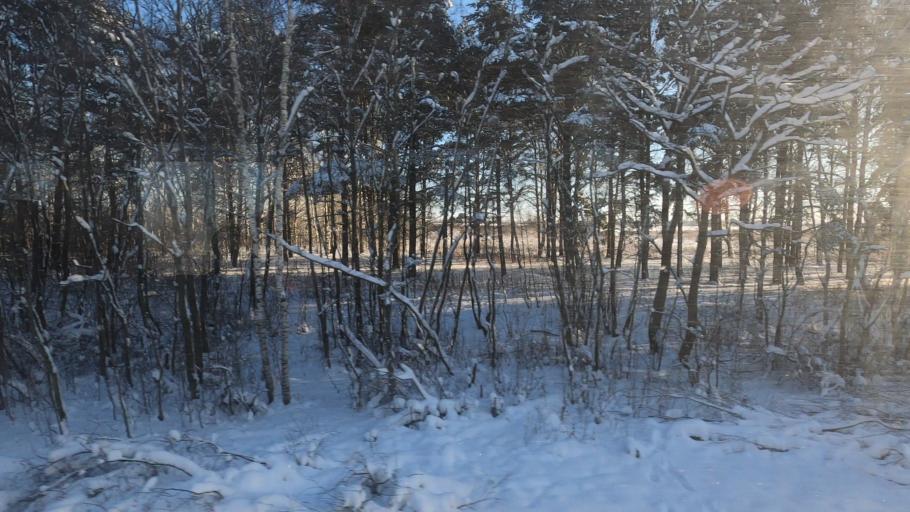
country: RU
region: Moskovskaya
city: Orud'yevo
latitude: 56.4330
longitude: 37.5021
